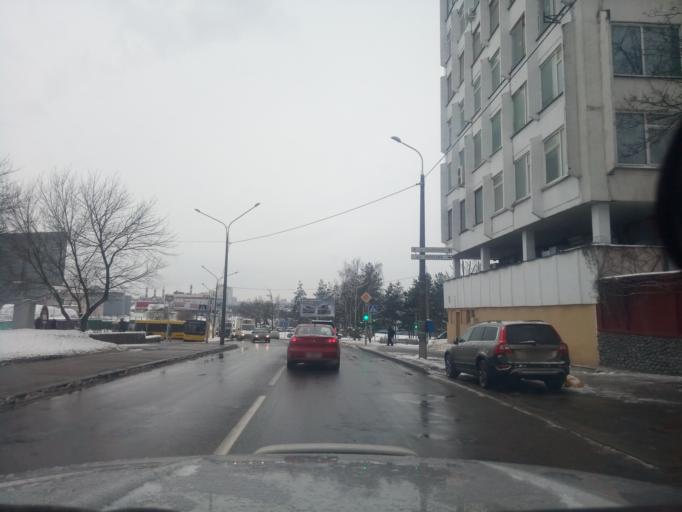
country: BY
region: Minsk
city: Minsk
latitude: 53.8920
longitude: 27.5860
